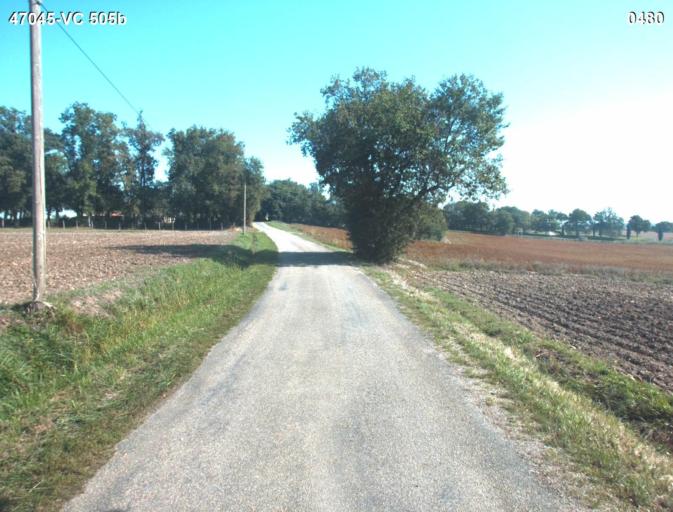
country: FR
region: Aquitaine
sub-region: Departement du Lot-et-Garonne
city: Nerac
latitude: 44.1486
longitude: 0.3970
